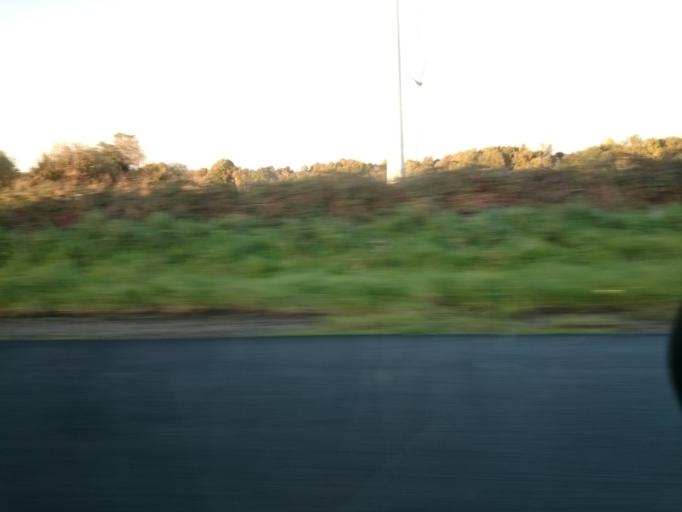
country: FR
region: Brittany
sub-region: Departement du Finistere
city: Plouigneau
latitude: 48.5758
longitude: -3.6948
